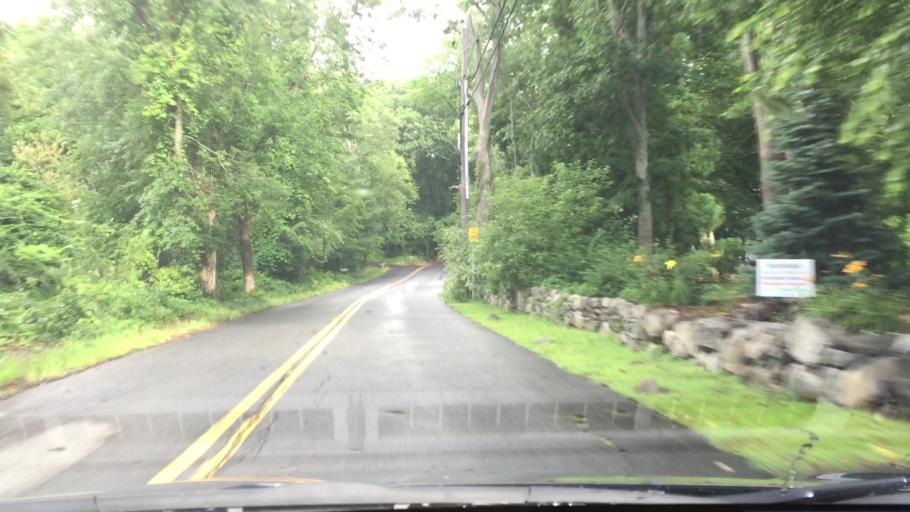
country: US
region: Massachusetts
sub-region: Middlesex County
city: Acton
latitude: 42.5059
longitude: -71.4473
